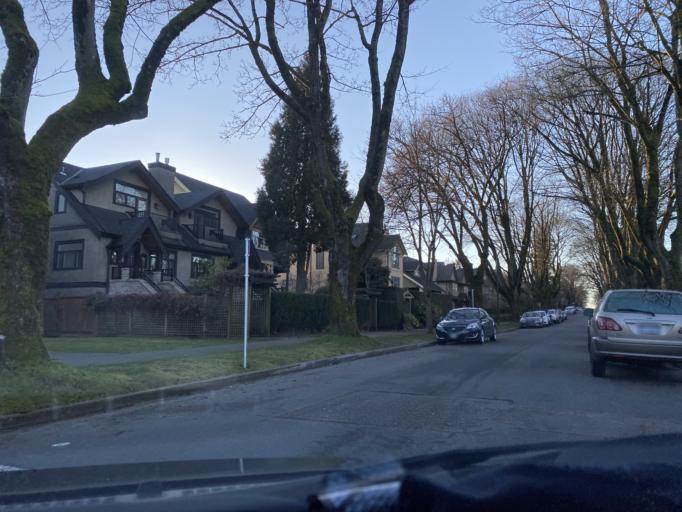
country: CA
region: British Columbia
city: West End
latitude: 49.2618
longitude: -123.1459
